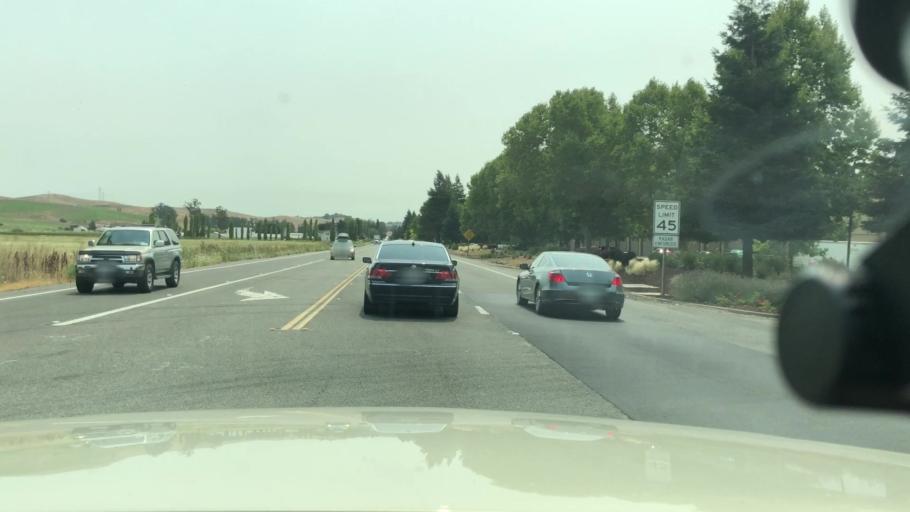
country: US
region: California
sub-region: Sonoma County
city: Petaluma
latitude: 38.2331
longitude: -122.5875
